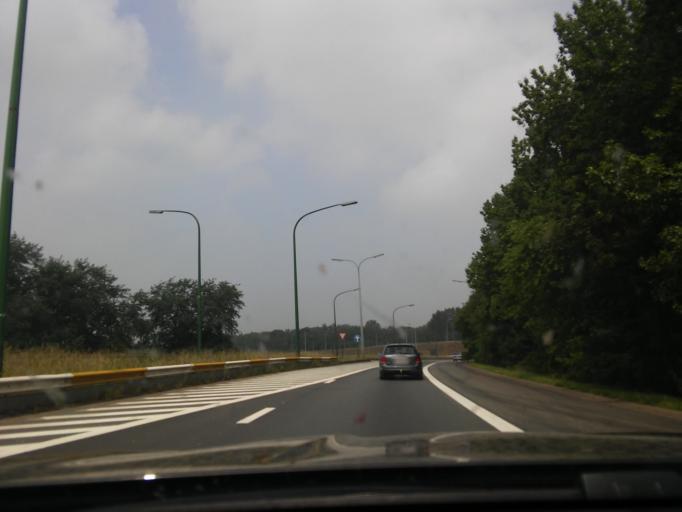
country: BE
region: Flanders
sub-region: Provincie Antwerpen
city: Zwijndrecht
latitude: 51.2174
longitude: 4.3534
